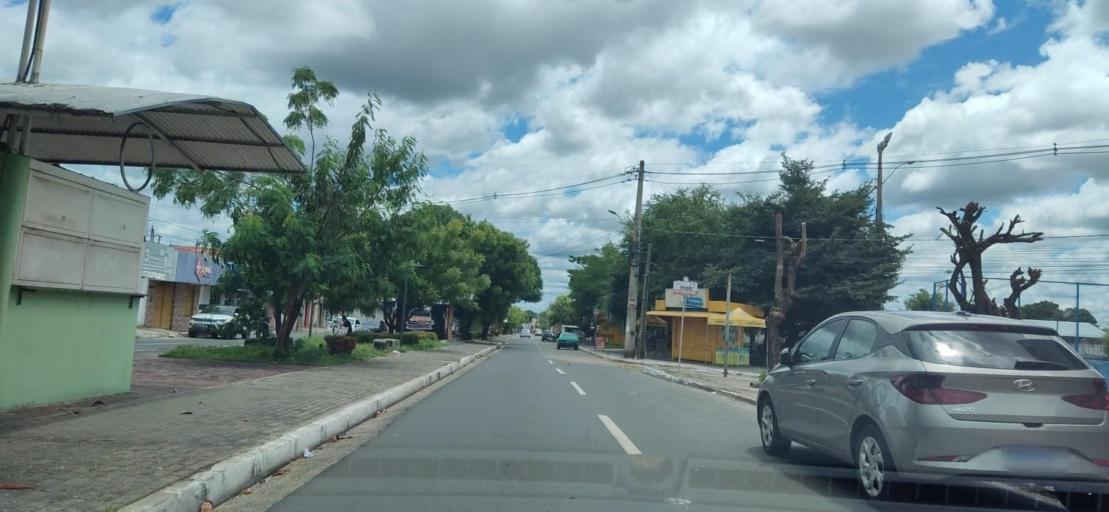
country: BR
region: Piaui
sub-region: Teresina
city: Teresina
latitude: -5.1491
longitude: -42.7826
